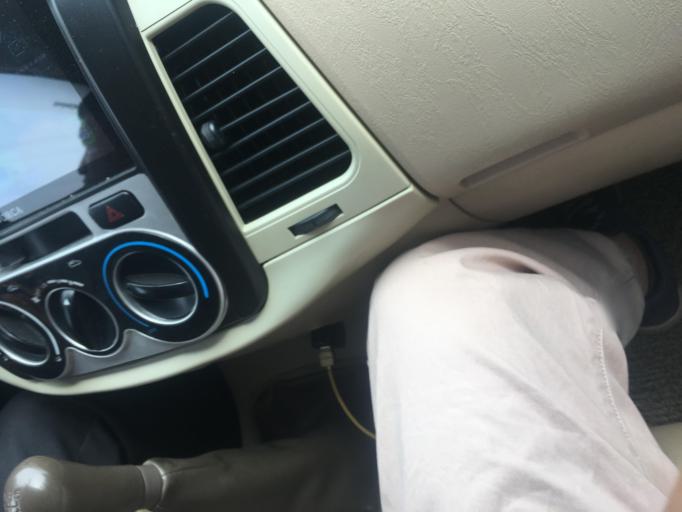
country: VN
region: Lang Son
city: Binh Gia
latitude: 22.1360
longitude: 106.3387
